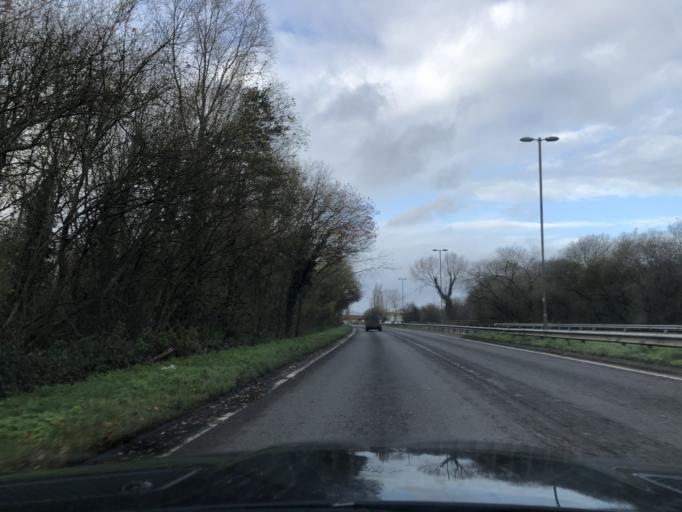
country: GB
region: England
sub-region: Surrey
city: Frimley
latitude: 51.3259
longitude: -0.7664
